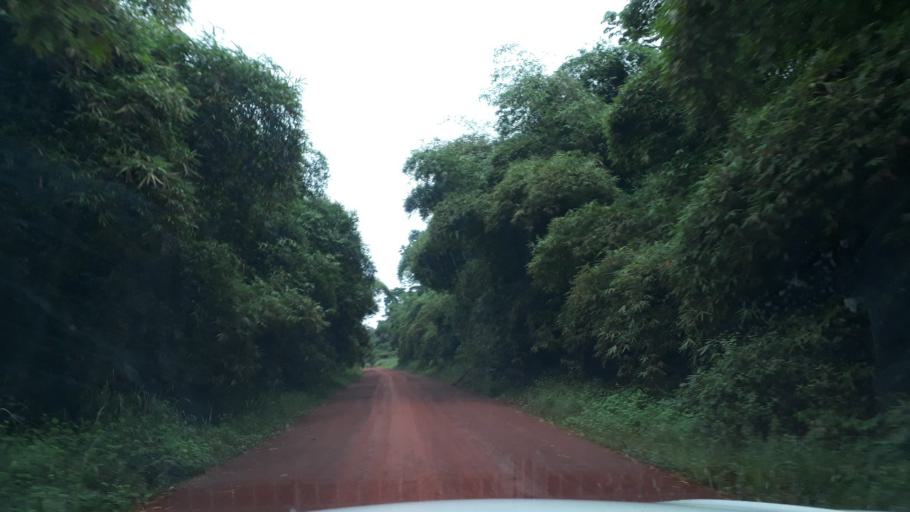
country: CD
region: Eastern Province
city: Wamba
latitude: 1.3601
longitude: 27.5931
